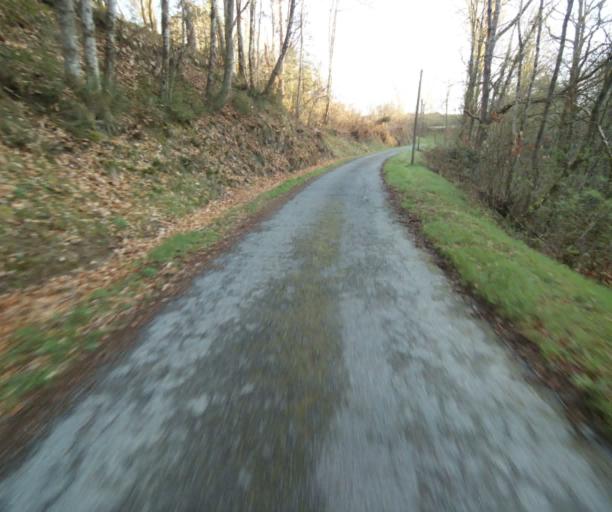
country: FR
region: Limousin
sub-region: Departement de la Correze
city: Correze
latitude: 45.3754
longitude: 1.8480
